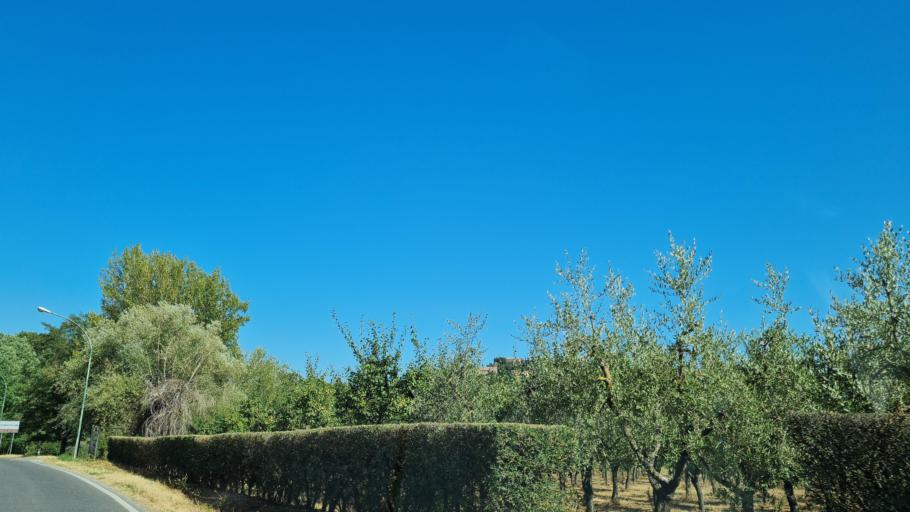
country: IT
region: Tuscany
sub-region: Provincia di Siena
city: Montepulciano
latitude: 43.0808
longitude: 11.7809
